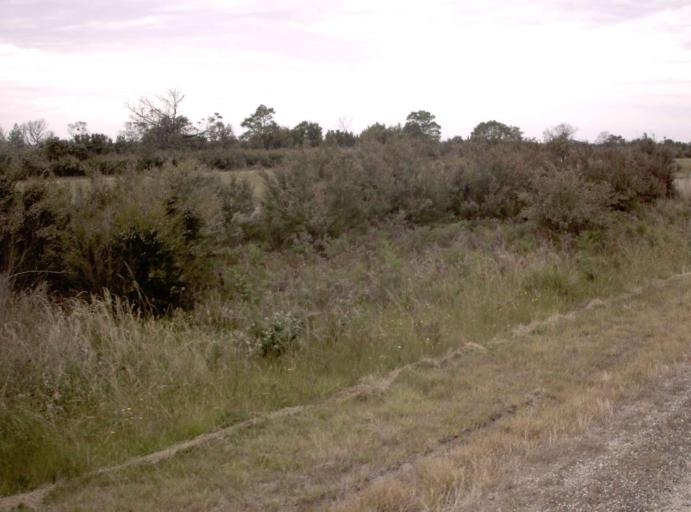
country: AU
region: Victoria
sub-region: Wellington
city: Sale
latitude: -38.1832
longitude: 147.2597
